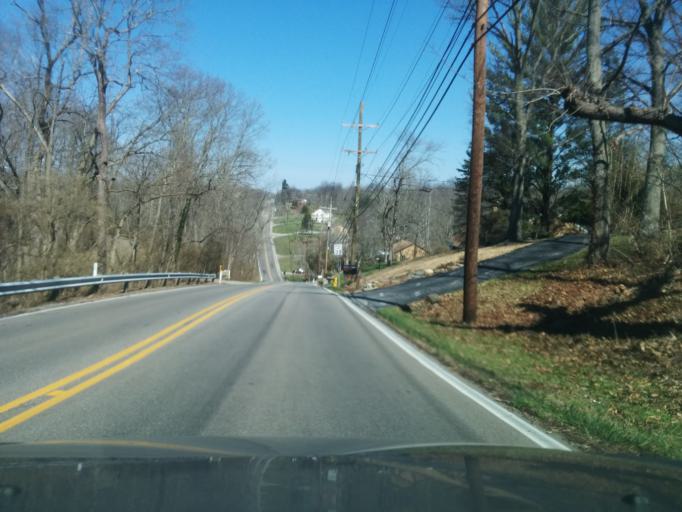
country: US
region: Ohio
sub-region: Hamilton County
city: Dent
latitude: 39.1827
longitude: -84.6283
